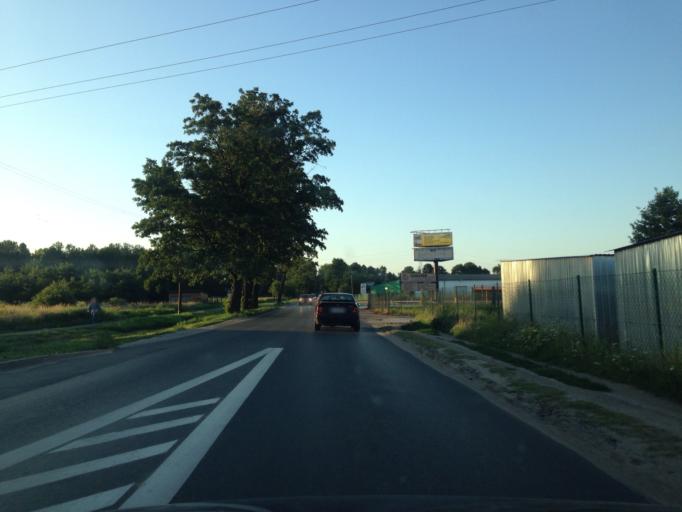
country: PL
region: Kujawsko-Pomorskie
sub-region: Powiat torunski
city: Lubicz Dolny
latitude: 53.0312
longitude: 18.6739
